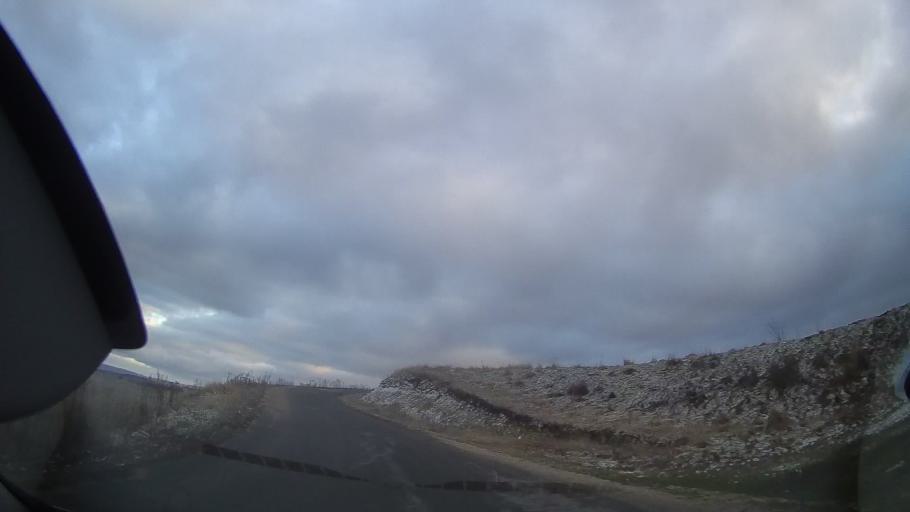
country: RO
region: Cluj
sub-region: Comuna Manastireni
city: Manastireni
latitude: 46.7791
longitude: 23.0549
